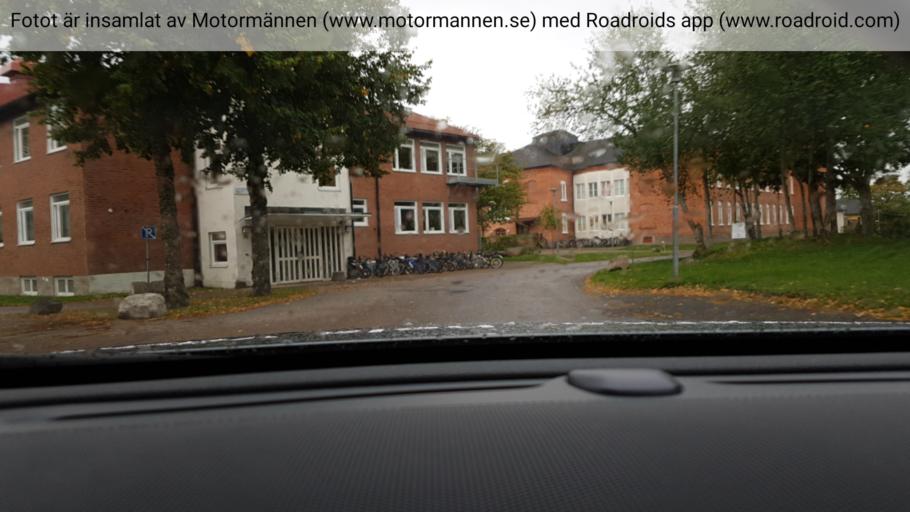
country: SE
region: Vaestra Goetaland
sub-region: Vanersborgs Kommun
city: Vargon
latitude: 58.3417
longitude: 12.3574
